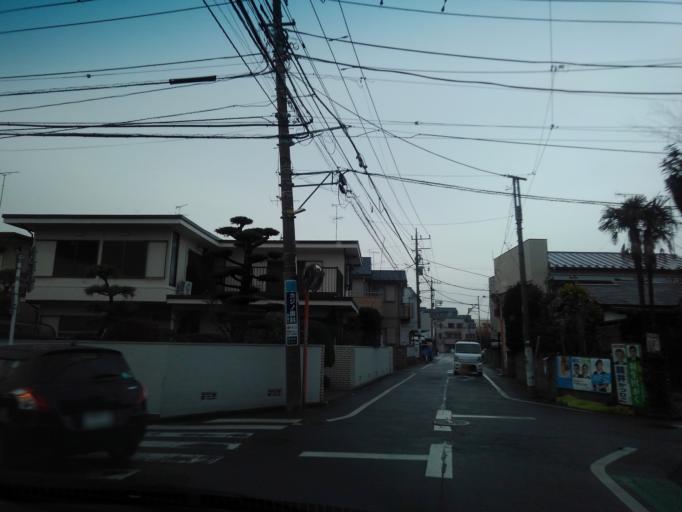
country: JP
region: Tokyo
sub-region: Machida-shi
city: Machida
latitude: 35.5166
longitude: 139.4403
